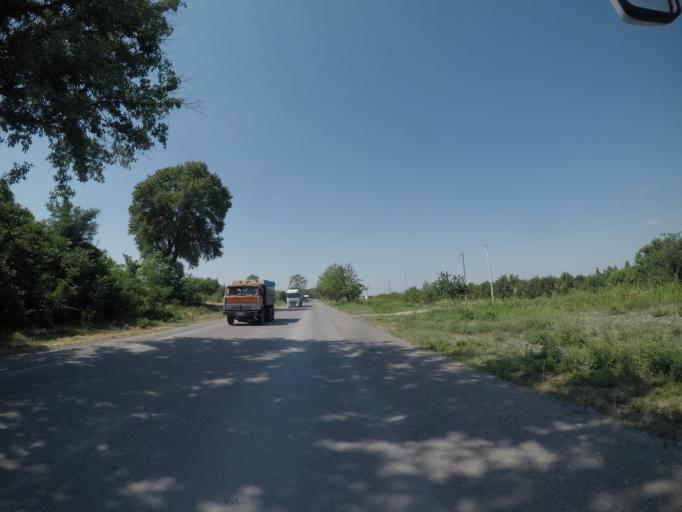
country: AZ
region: Agdas
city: Agdas
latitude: 40.6967
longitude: 47.5411
